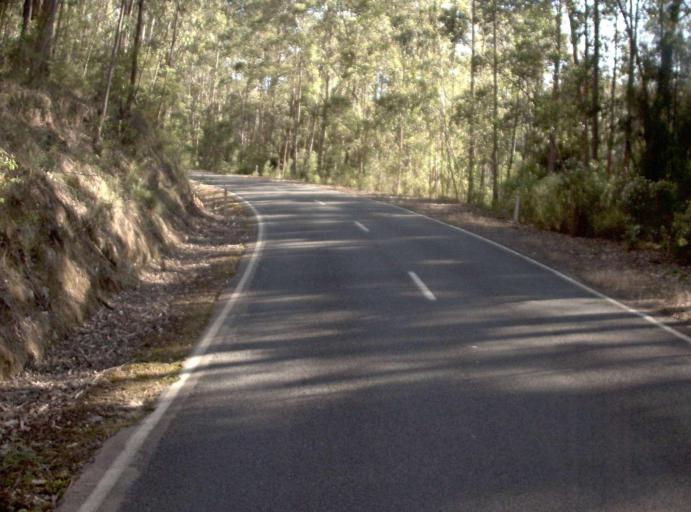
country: AU
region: Victoria
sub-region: East Gippsland
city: Lakes Entrance
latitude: -37.6483
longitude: 148.4814
